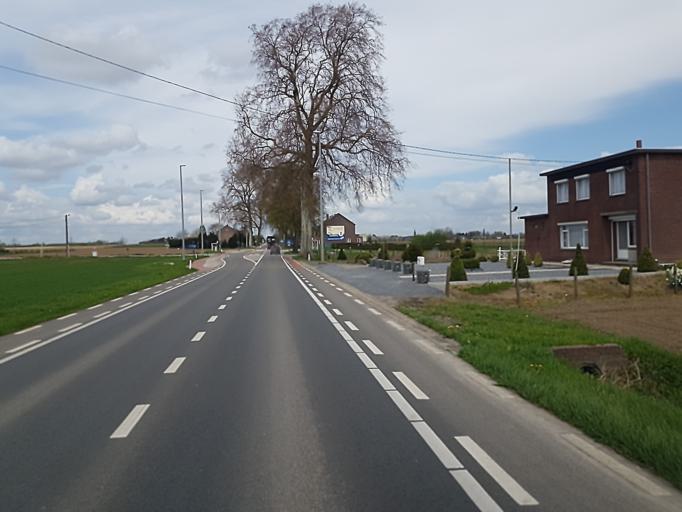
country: BE
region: Flanders
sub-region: Provincie Limburg
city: Riemst
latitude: 50.8274
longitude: 5.6257
